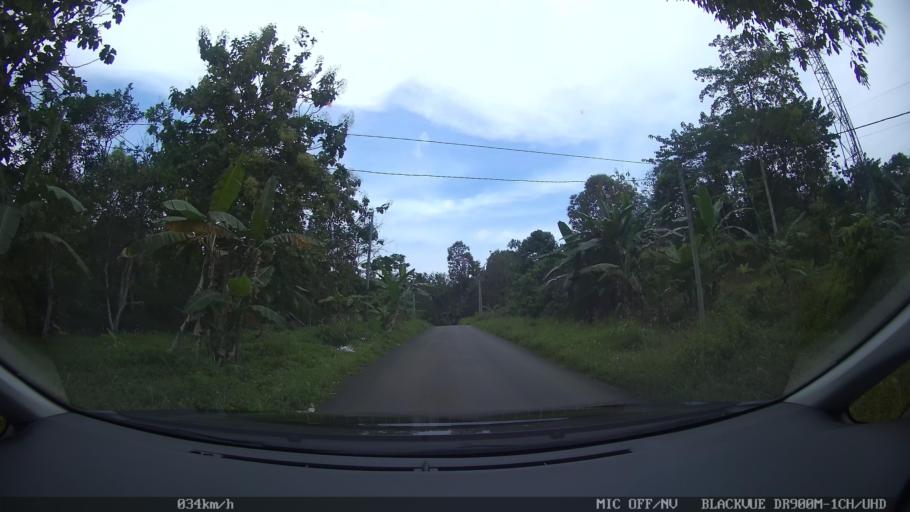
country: ID
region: Lampung
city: Kedaton
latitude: -5.3954
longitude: 105.1910
